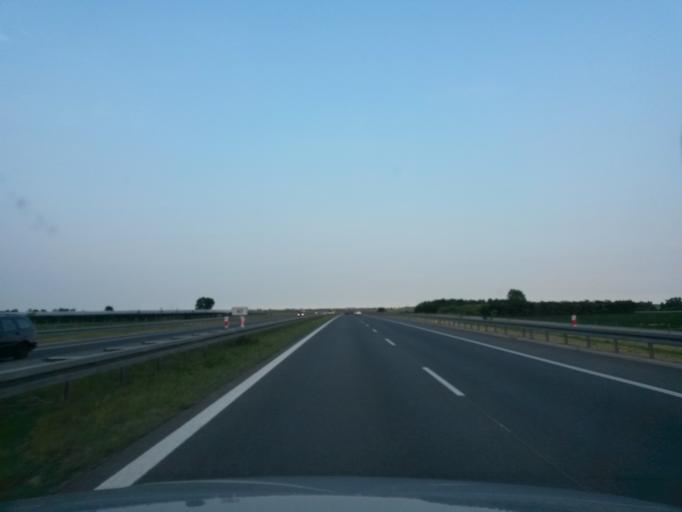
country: PL
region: Lower Silesian Voivodeship
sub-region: Powiat olesnicki
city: Dobroszyce
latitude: 51.2231
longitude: 17.3039
